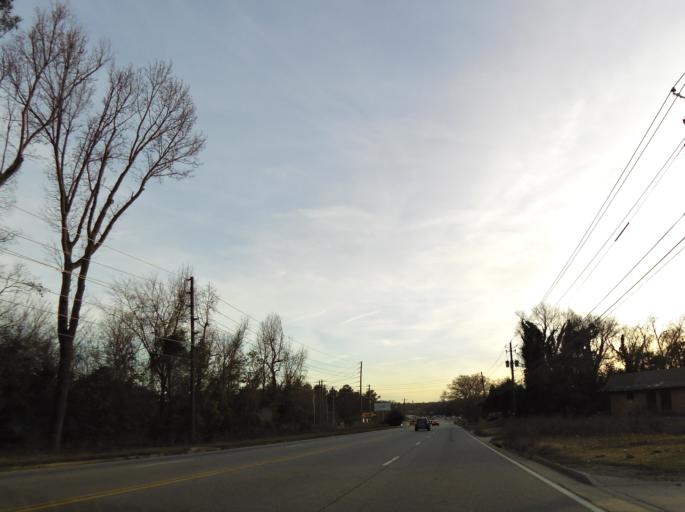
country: US
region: Georgia
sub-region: Bibb County
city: Macon
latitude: 32.7760
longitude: -83.6573
